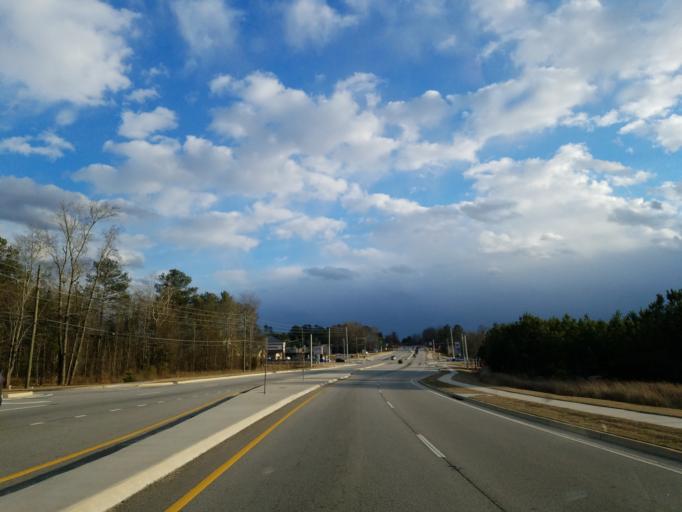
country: US
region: Georgia
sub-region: Henry County
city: Stockbridge
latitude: 33.5206
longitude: -84.1920
